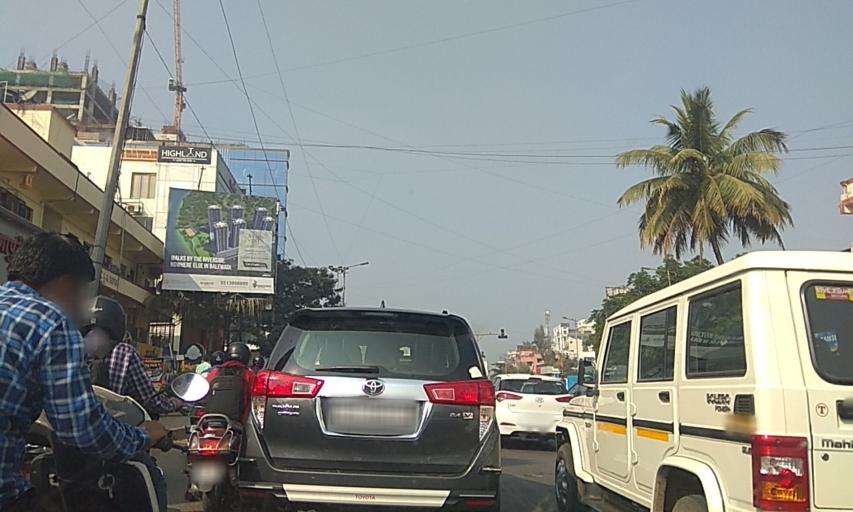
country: IN
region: Maharashtra
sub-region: Pune Division
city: Pimpri
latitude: 18.5641
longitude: 73.7778
